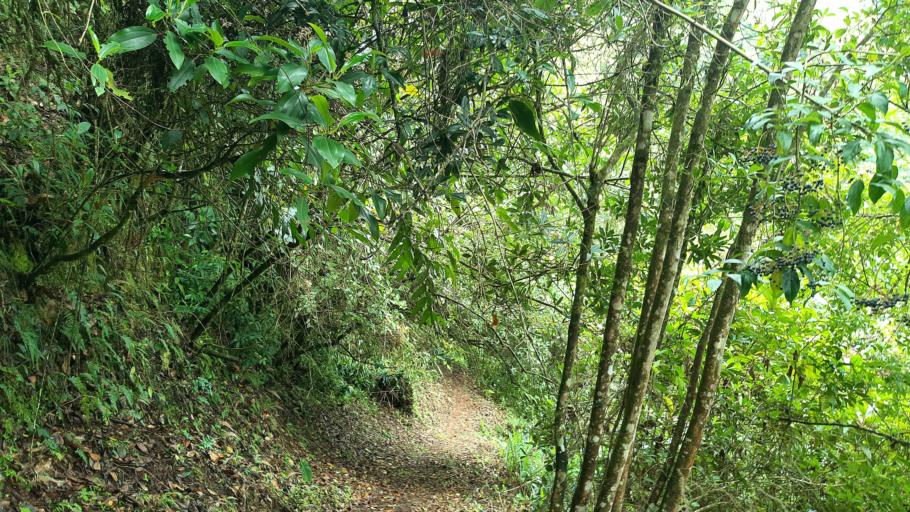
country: CO
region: Boyaca
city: Santa Maria
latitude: 4.9112
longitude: -73.2996
